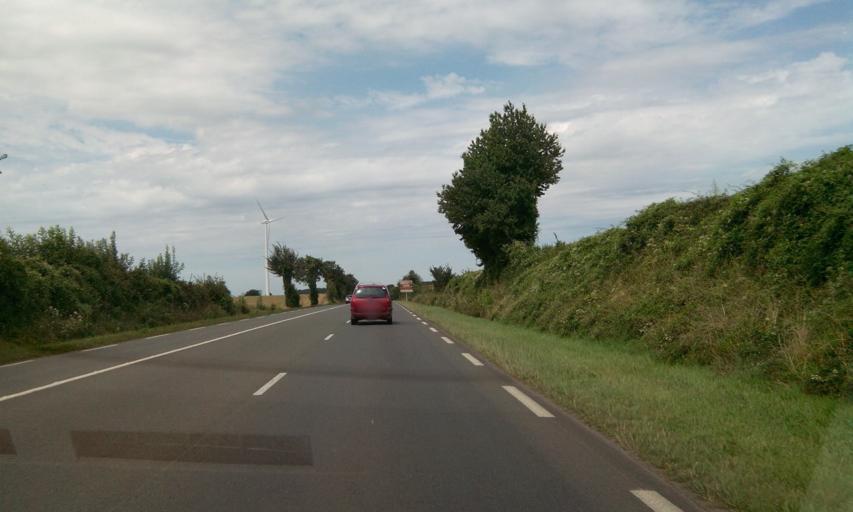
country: FR
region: Poitou-Charentes
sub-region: Departement des Deux-Sevres
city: Melle
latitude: 46.2338
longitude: -0.1681
